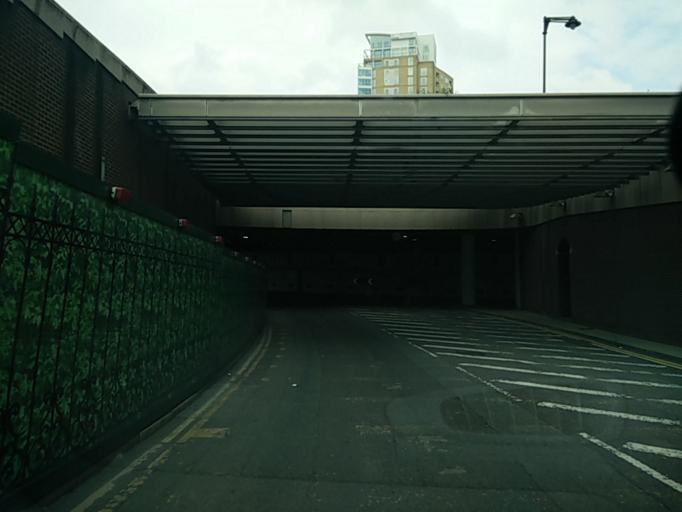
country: GB
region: England
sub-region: Greater London
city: Poplar
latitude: 51.5046
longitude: -0.0260
